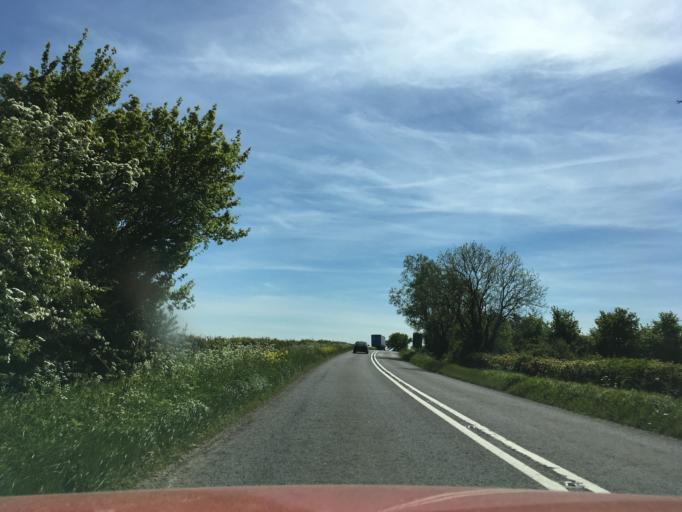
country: GB
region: England
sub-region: Wiltshire
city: Hankerton
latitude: 51.6524
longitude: -2.0558
